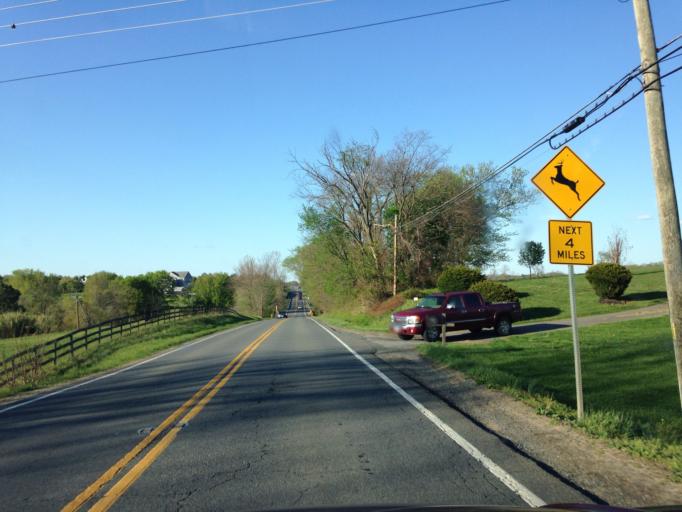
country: US
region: Virginia
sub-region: Loudoun County
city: Lovettsville
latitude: 39.2056
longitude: -77.6697
